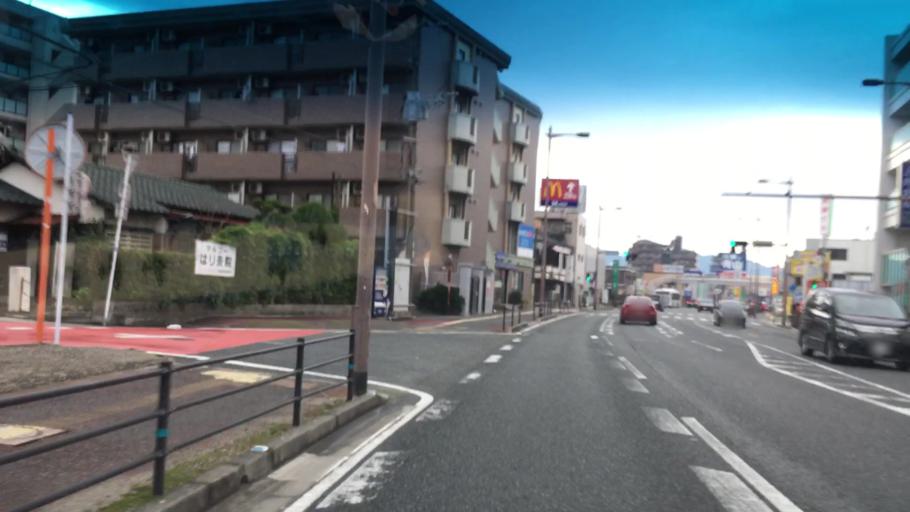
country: JP
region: Fukuoka
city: Fukuoka-shi
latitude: 33.5684
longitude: 130.3520
